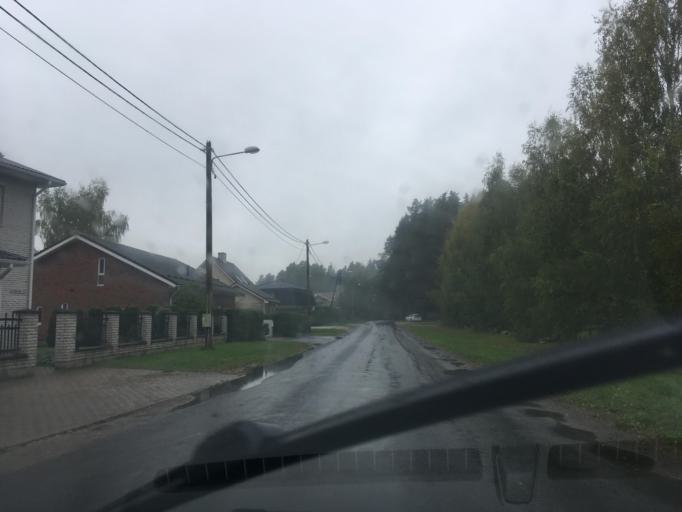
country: EE
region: Tartu
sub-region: Tartu linn
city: Tartu
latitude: 58.3591
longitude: 26.7906
